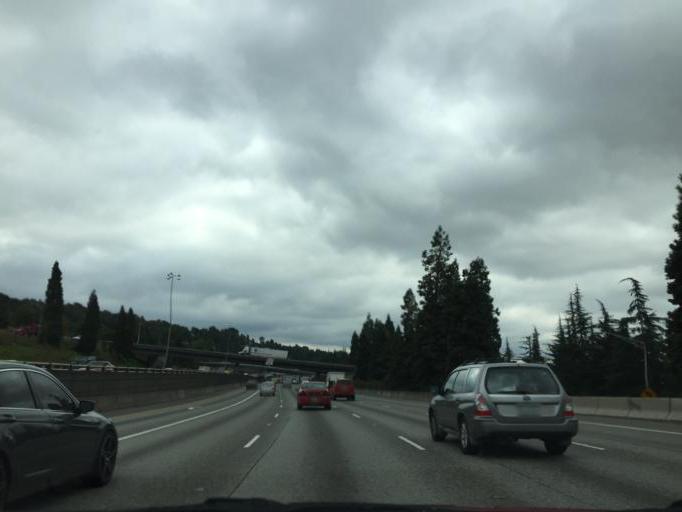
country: US
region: Washington
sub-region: King County
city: White Center
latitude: 47.5507
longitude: -122.3160
